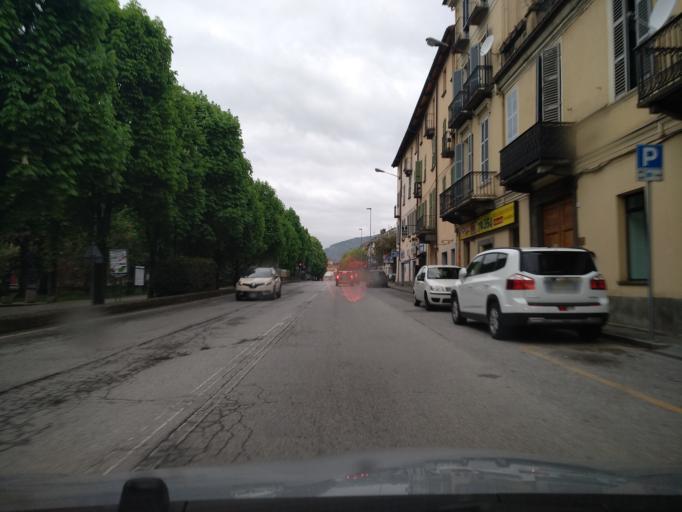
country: IT
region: Piedmont
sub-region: Provincia di Torino
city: Pinerolo
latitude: 44.8850
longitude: 7.3275
